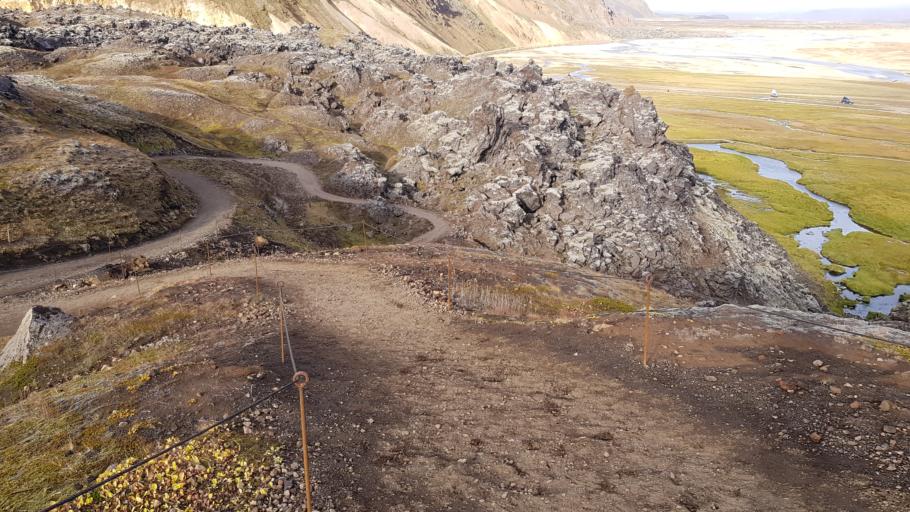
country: IS
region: South
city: Vestmannaeyjar
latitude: 63.9903
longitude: -19.0653
